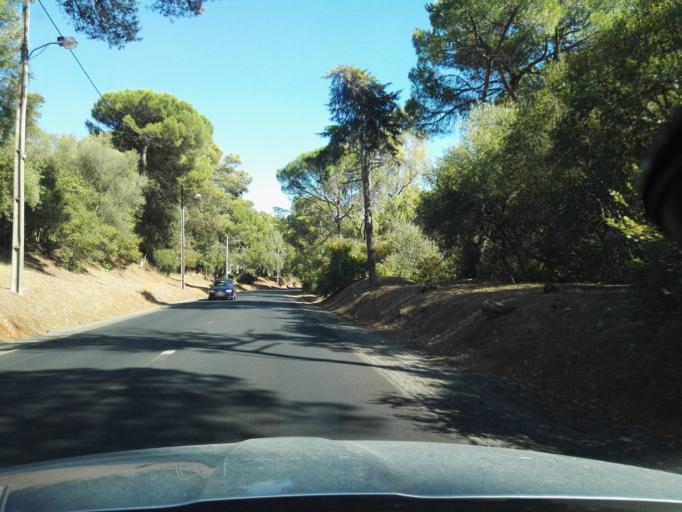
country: PT
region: Lisbon
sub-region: Odivelas
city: Pontinha
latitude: 38.7276
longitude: -9.1960
